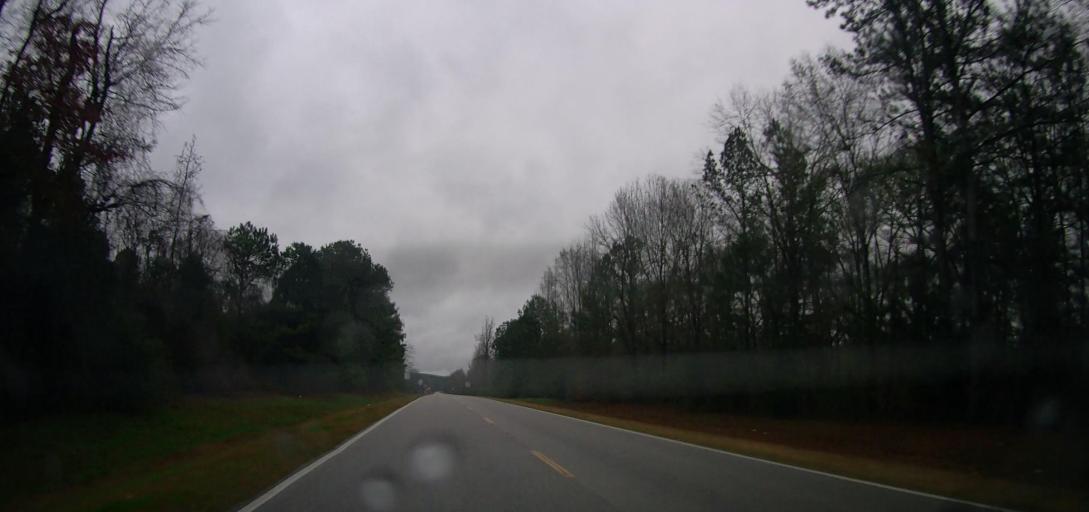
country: US
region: Alabama
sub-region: Bibb County
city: Centreville
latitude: 32.9272
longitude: -87.0474
